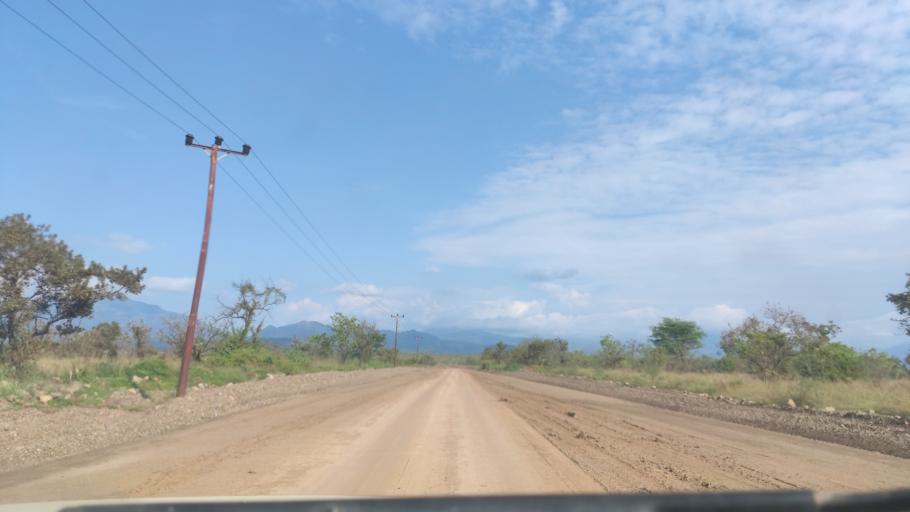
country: ET
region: Southern Nations, Nationalities, and People's Region
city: Felege Neway
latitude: 6.4260
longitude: 37.2303
